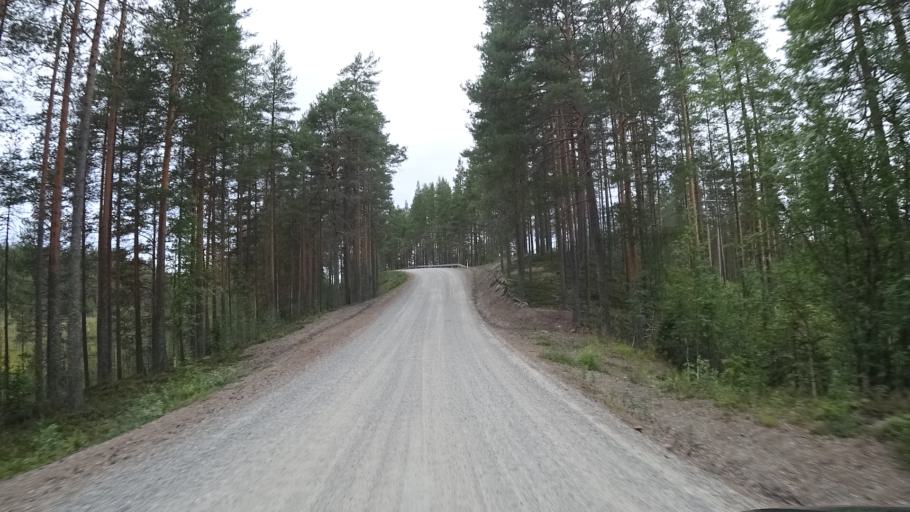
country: FI
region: North Karelia
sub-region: Pielisen Karjala
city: Lieksa
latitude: 63.2365
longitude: 30.3609
